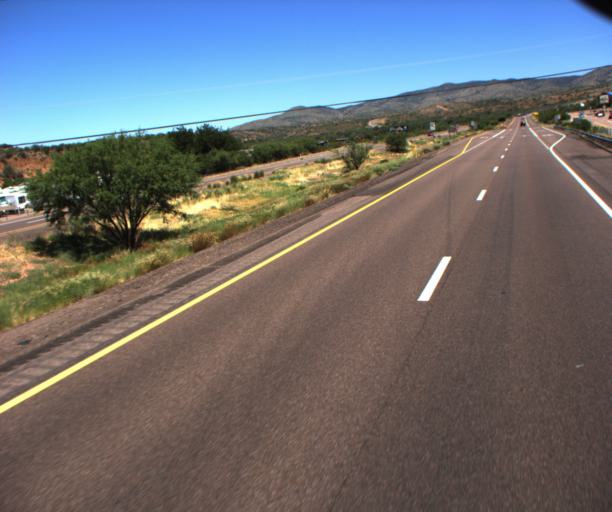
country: US
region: Arizona
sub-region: Gila County
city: Payson
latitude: 34.1057
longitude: -111.3535
